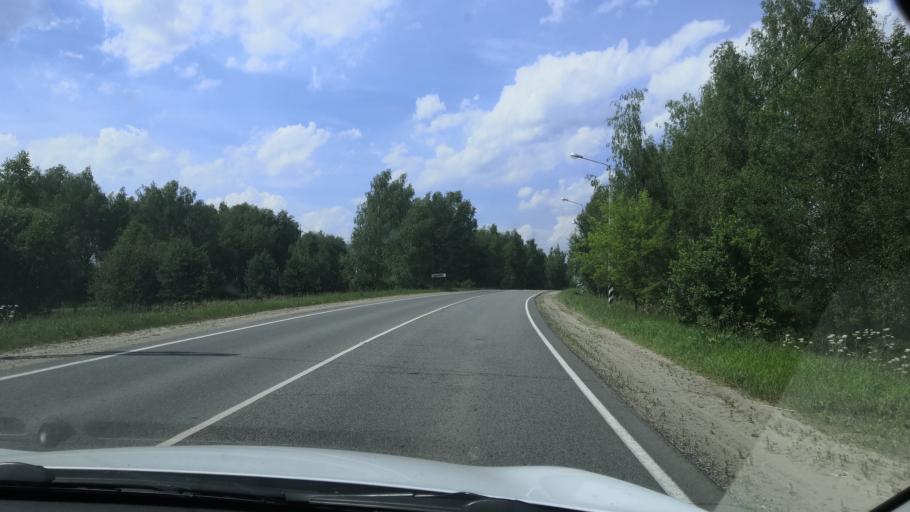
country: RU
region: Rjazan
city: Murmino
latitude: 54.5951
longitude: 40.0918
